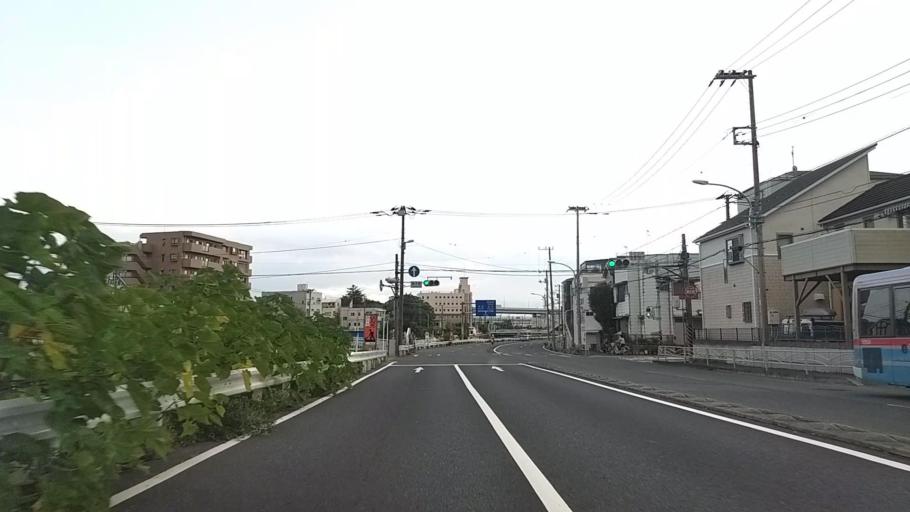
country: JP
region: Kanagawa
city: Yokohama
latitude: 35.4176
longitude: 139.6265
